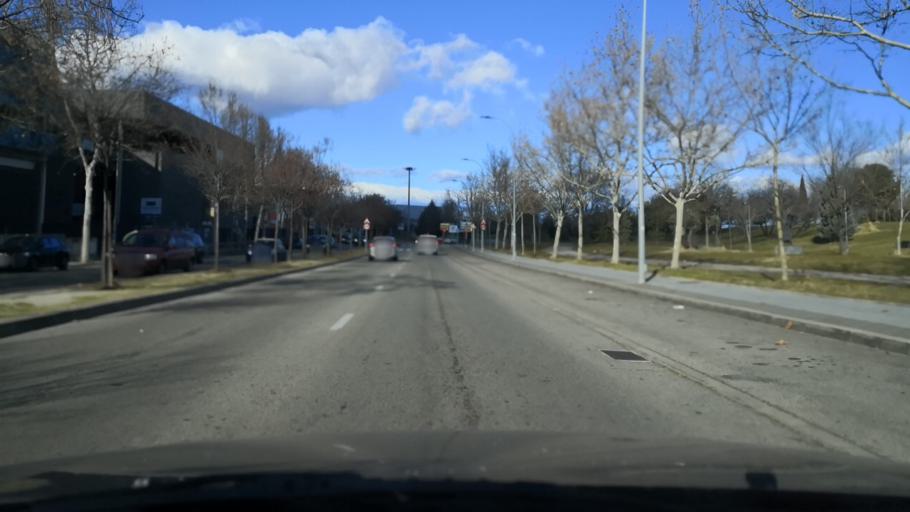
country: ES
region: Madrid
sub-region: Provincia de Madrid
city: San Sebastian de los Reyes
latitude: 40.5509
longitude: -3.6100
